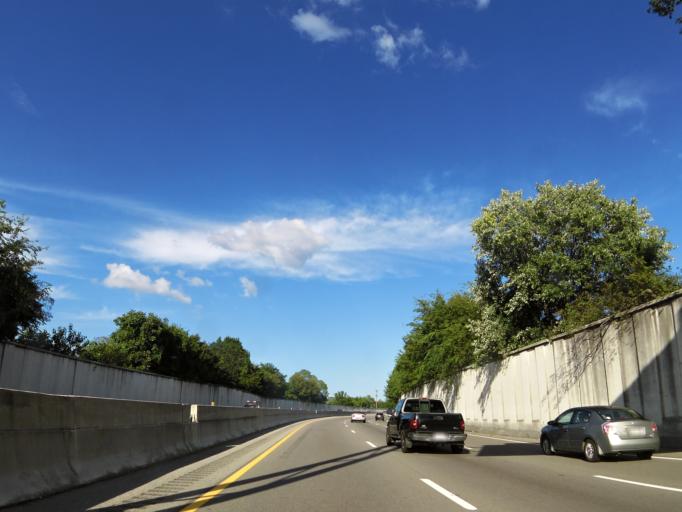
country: US
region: Tennessee
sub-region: Davidson County
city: Nashville
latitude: 36.2394
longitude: -86.7762
